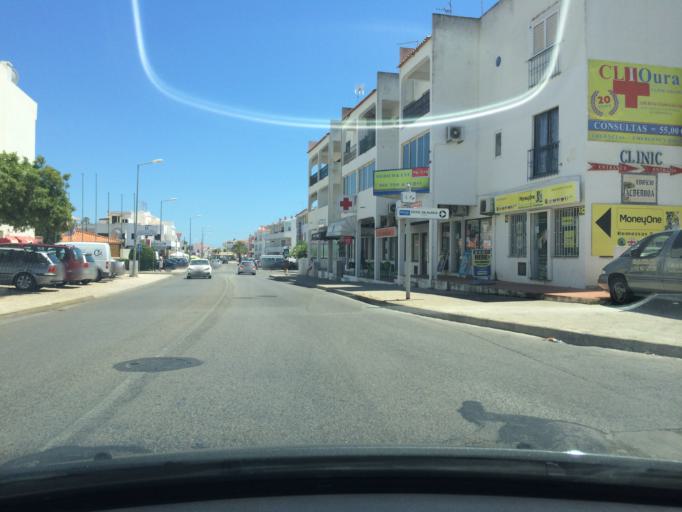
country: PT
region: Faro
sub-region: Albufeira
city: Albufeira
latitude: 37.0940
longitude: -8.2240
